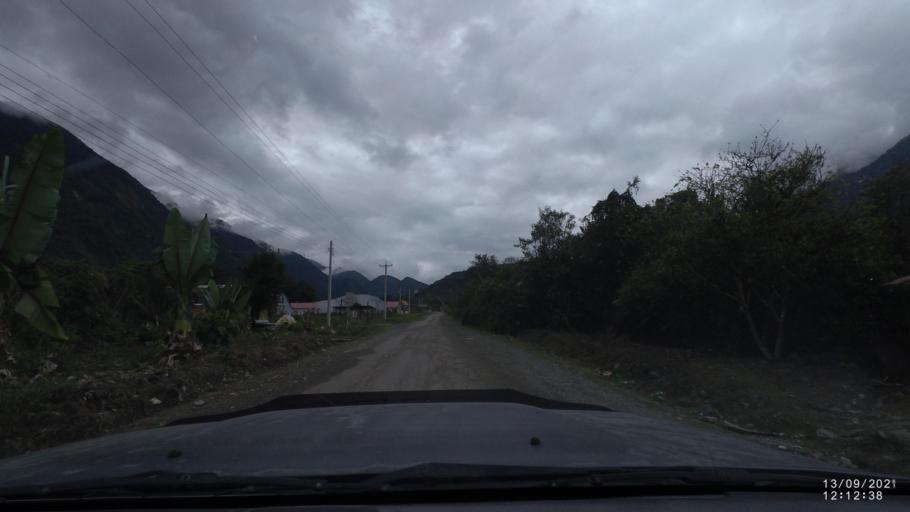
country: BO
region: Cochabamba
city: Colomi
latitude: -17.2167
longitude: -65.8235
